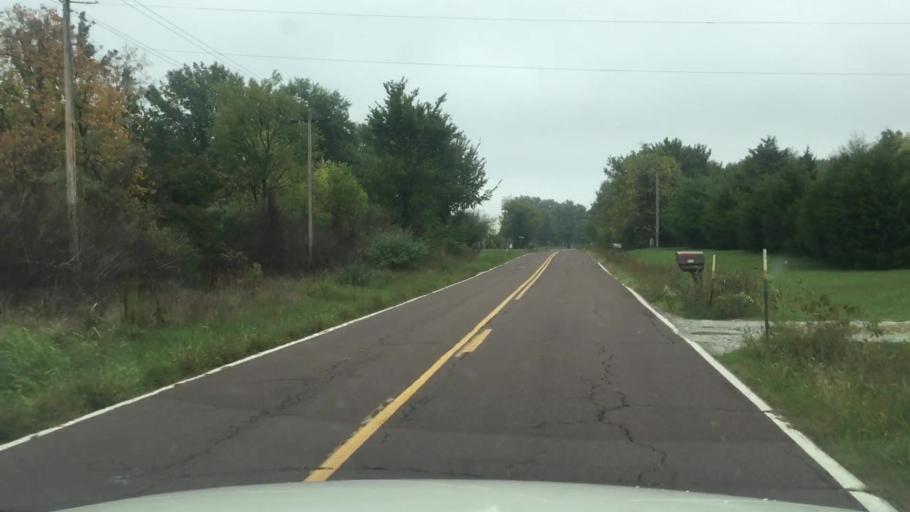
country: US
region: Missouri
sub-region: Boone County
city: Ashland
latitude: 38.8349
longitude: -92.3476
